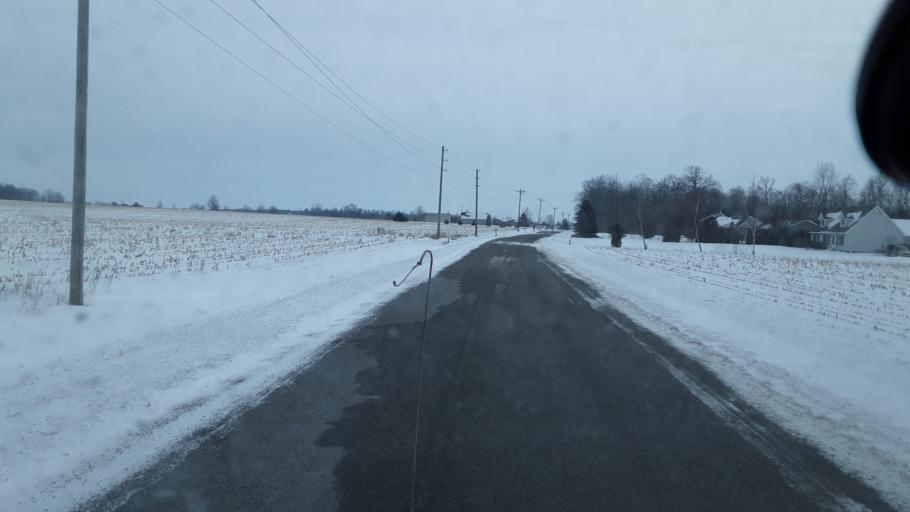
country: US
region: Ohio
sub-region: Union County
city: Marysville
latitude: 40.1772
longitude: -83.3747
